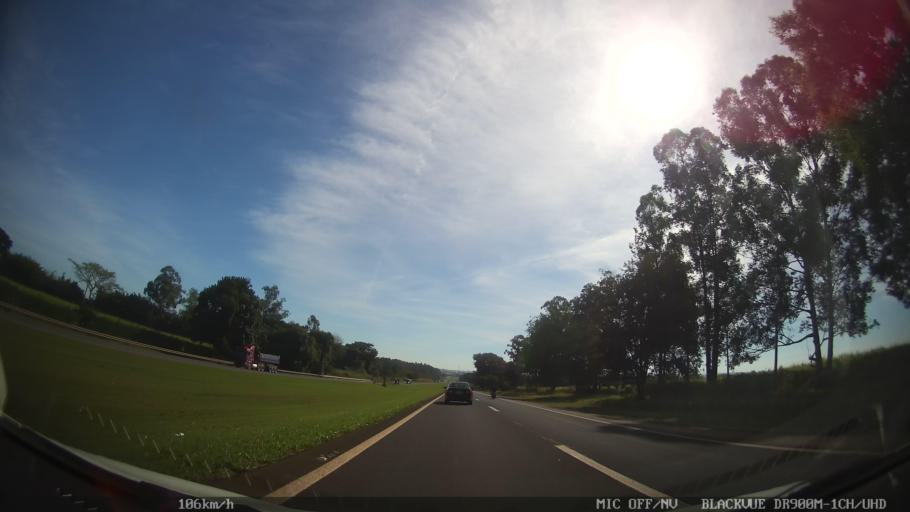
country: BR
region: Sao Paulo
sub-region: Leme
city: Leme
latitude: -22.2392
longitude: -47.3907
